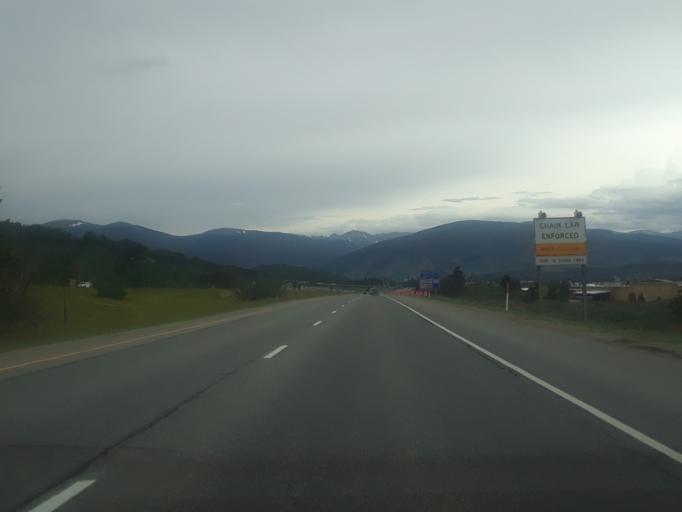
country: US
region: Colorado
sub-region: Summit County
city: Frisco
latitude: 39.5874
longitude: -106.1044
